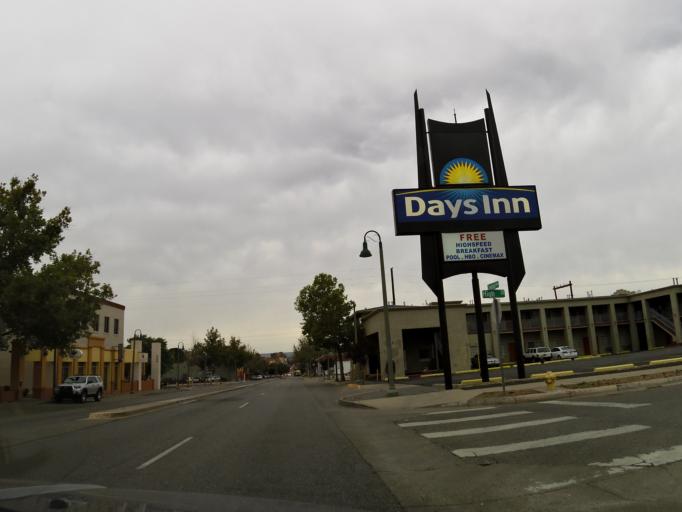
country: US
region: New Mexico
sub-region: Bernalillo County
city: Albuquerque
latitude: 35.0831
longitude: -106.6397
